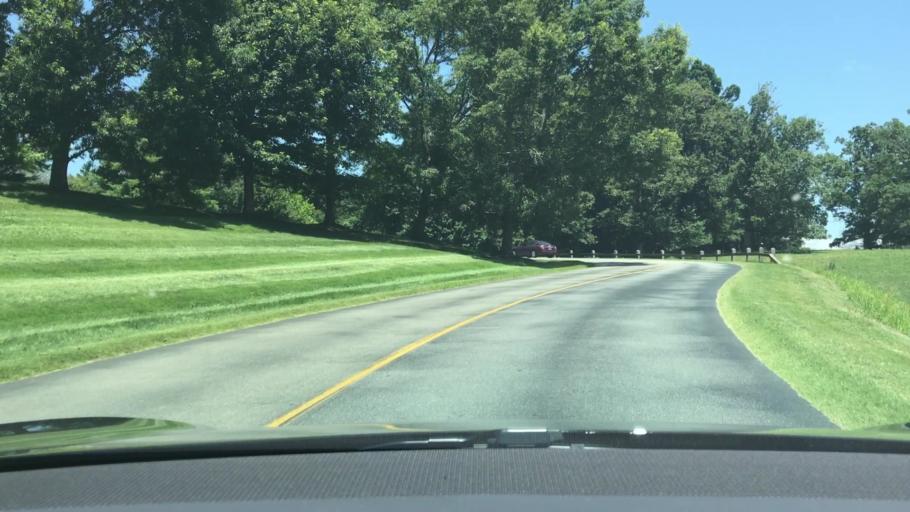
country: US
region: North Carolina
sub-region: Buncombe County
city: Asheville
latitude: 35.5579
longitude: -82.5773
